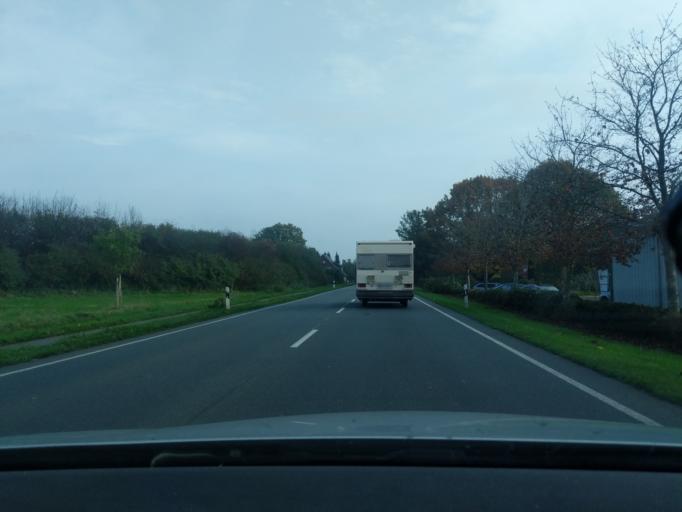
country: DE
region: Lower Saxony
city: Burweg
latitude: 53.6219
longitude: 9.2684
